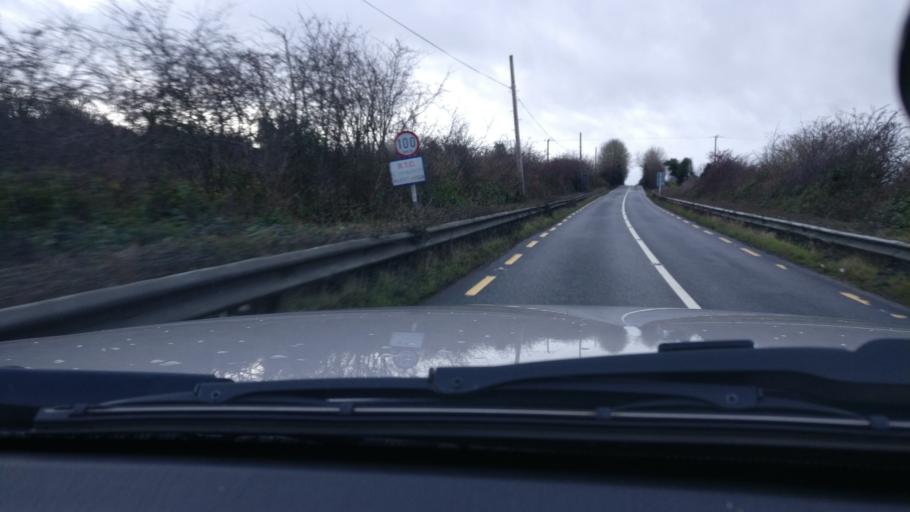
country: IE
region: Leinster
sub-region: An Iarmhi
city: Moate
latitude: 53.5832
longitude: -7.7302
